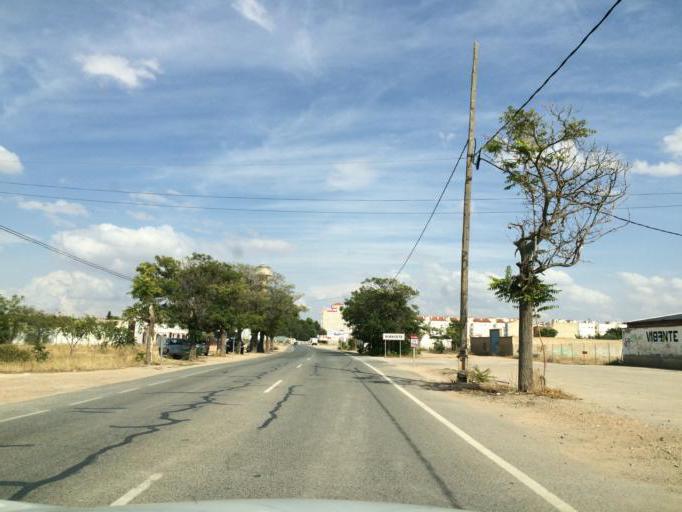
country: ES
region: Castille-La Mancha
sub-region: Provincia de Albacete
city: Albacete
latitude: 38.9977
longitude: -1.8813
